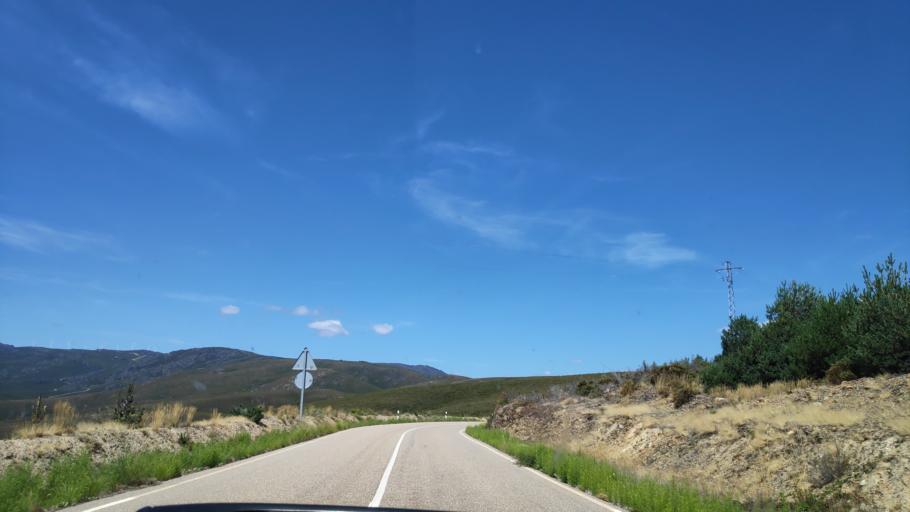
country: ES
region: Castille and Leon
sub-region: Provincia de Zamora
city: Requejo
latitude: 41.9998
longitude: -6.6907
